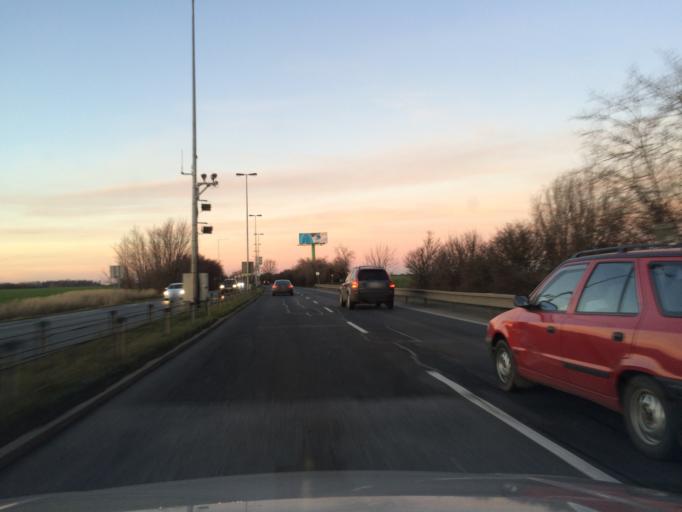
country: CZ
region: Central Bohemia
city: Tuchomerice
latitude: 50.1037
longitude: 14.2946
